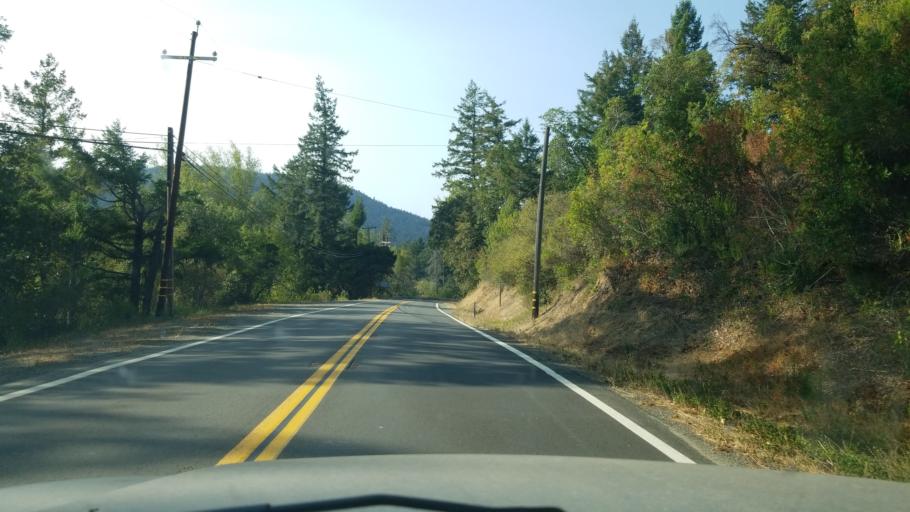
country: US
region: California
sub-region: Humboldt County
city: Redway
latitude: 40.2270
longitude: -123.8224
